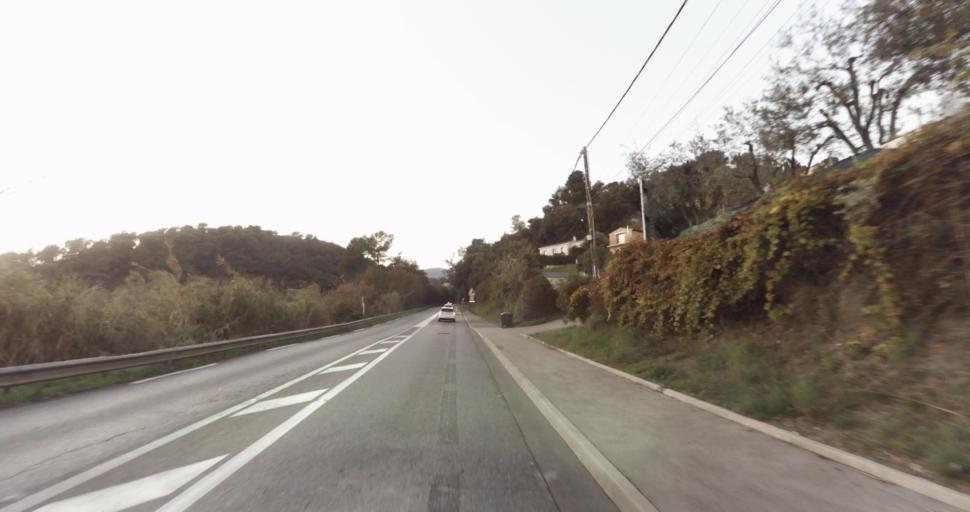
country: FR
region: Provence-Alpes-Cote d'Azur
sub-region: Departement des Alpes-Maritimes
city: Vence
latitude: 43.7130
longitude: 7.1217
